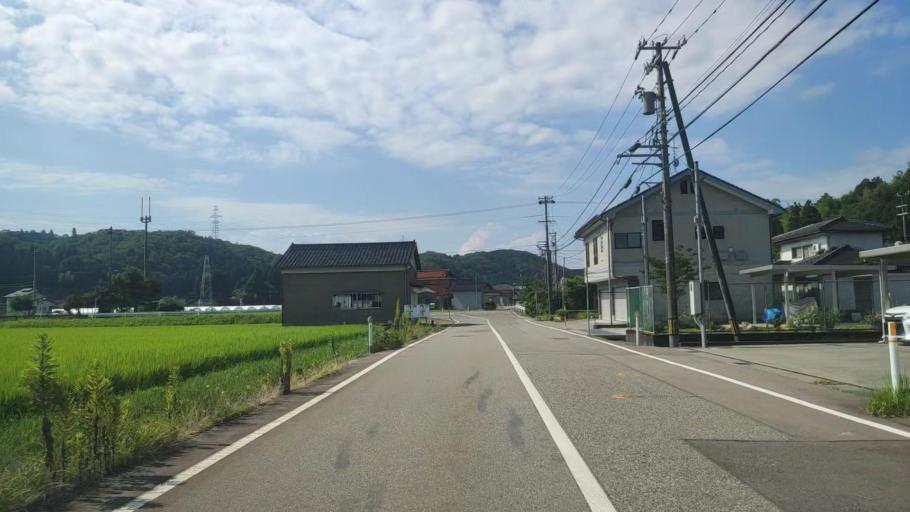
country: JP
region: Ishikawa
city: Komatsu
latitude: 36.3728
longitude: 136.4980
